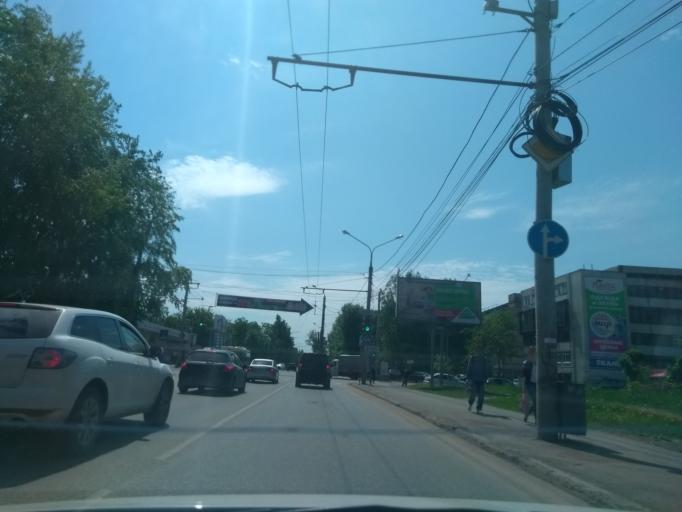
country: RU
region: Perm
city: Perm
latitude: 57.9825
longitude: 56.2467
